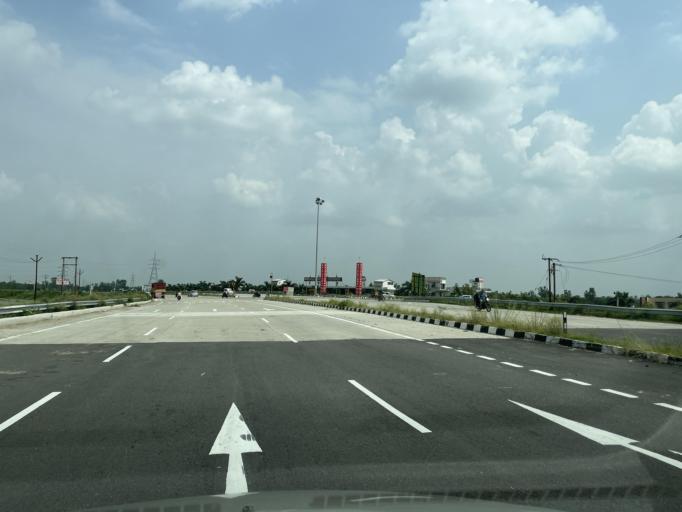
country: IN
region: Uttar Pradesh
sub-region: Bijnor
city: Dhampur
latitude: 29.3168
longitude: 78.5370
